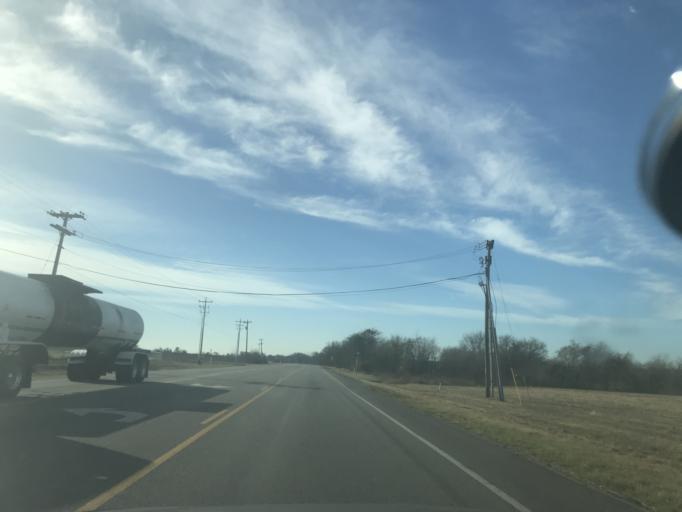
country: US
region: Texas
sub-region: Travis County
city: Manor
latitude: 30.3319
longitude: -97.5600
